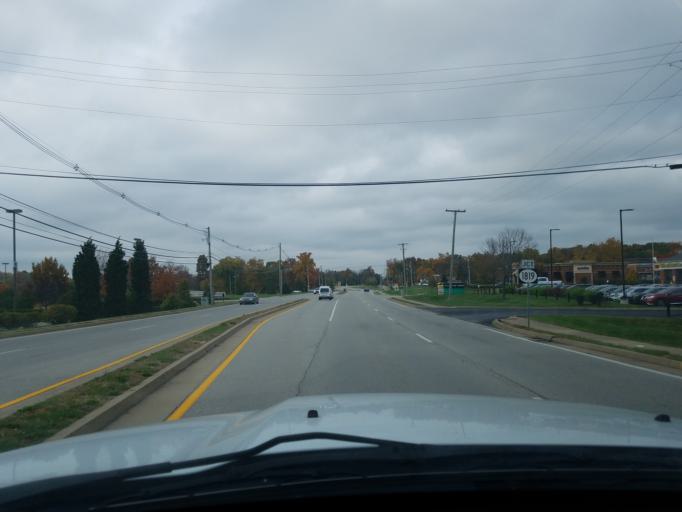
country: US
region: Kentucky
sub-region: Jefferson County
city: Douglass Hills
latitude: 38.2302
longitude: -85.5425
